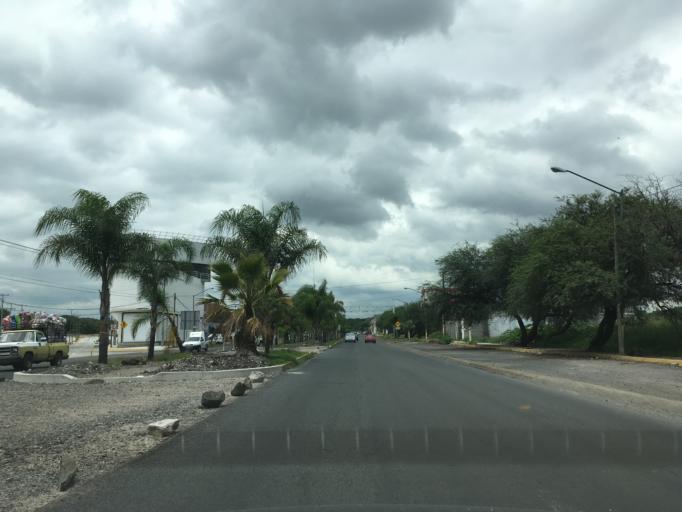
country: MX
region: Guanajuato
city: Moroleon
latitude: 20.1023
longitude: -101.1634
